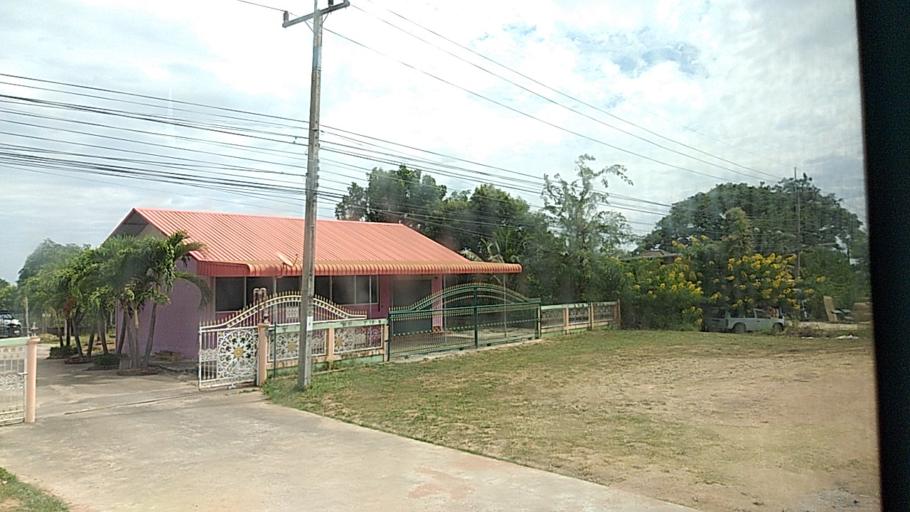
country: TH
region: Maha Sarakham
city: Chiang Yuen
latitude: 16.3660
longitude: 103.1065
